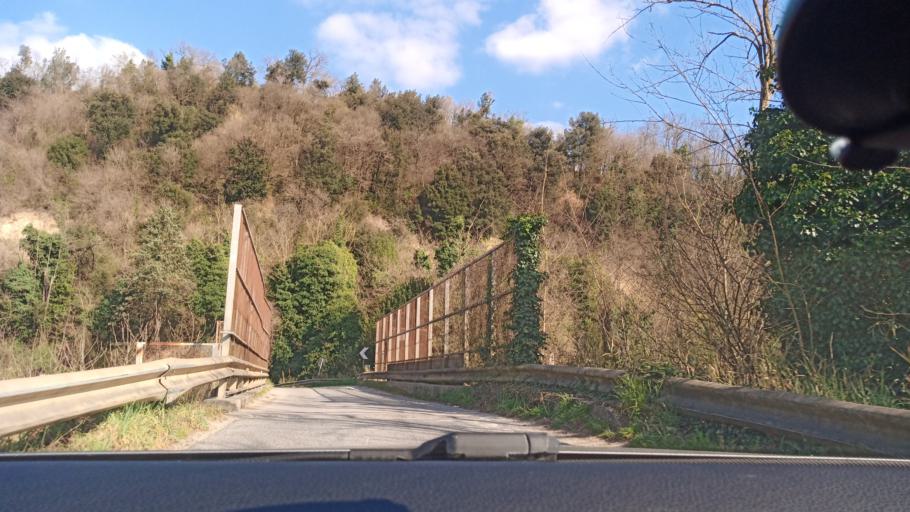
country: IT
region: Latium
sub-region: Citta metropolitana di Roma Capitale
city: Torrita Tiberina
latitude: 42.2353
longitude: 12.6317
